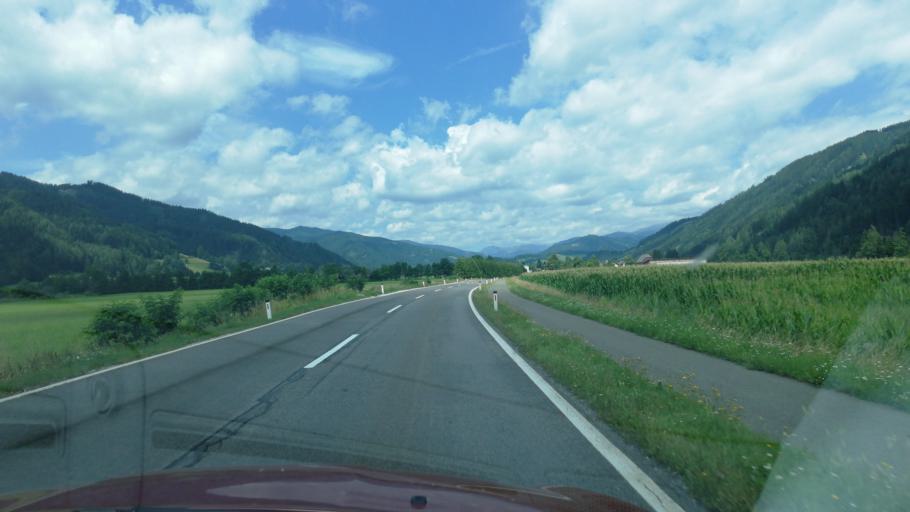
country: AT
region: Styria
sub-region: Politischer Bezirk Murtal
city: Oberkurzheim
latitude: 47.2377
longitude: 14.5391
